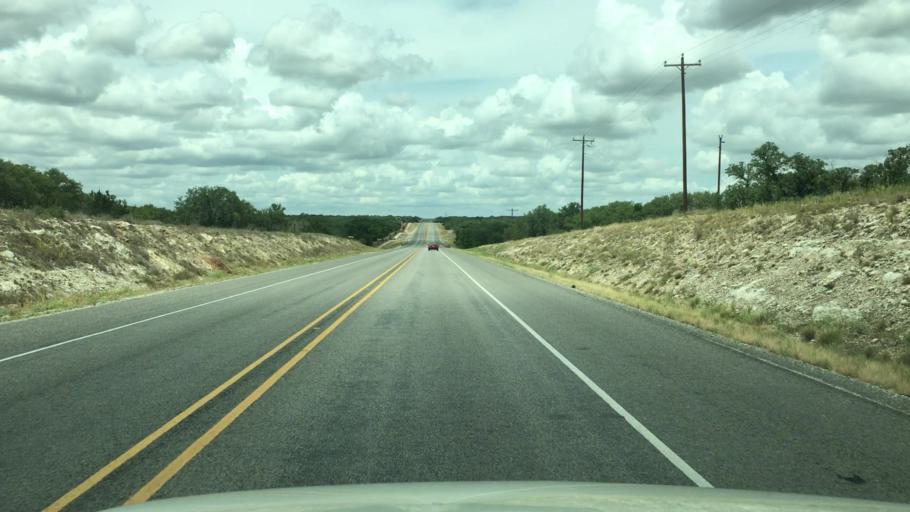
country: US
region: Texas
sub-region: McCulloch County
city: Brady
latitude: 31.0382
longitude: -99.2392
